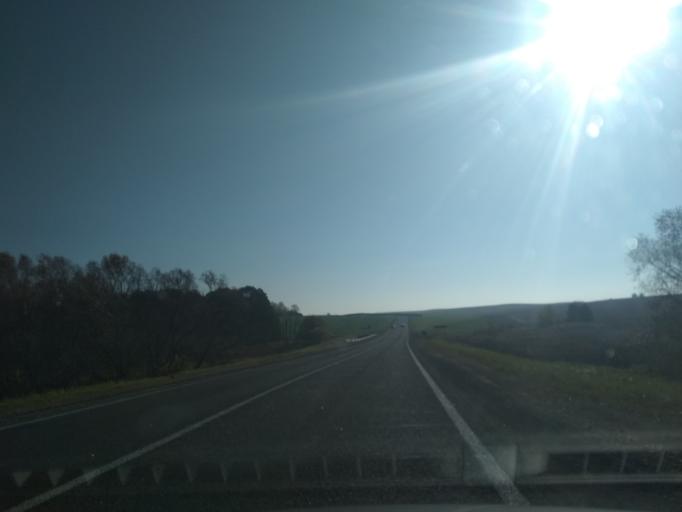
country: BY
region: Grodnenskaya
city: Zel'va
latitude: 53.1286
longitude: 25.0407
